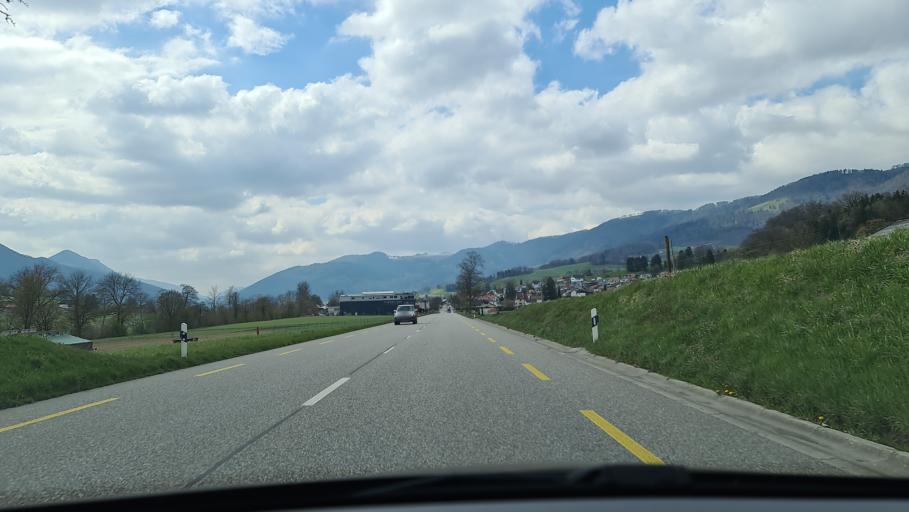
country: CH
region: Solothurn
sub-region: Bezirk Thal
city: Laupersdorf
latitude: 47.3122
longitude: 7.6699
